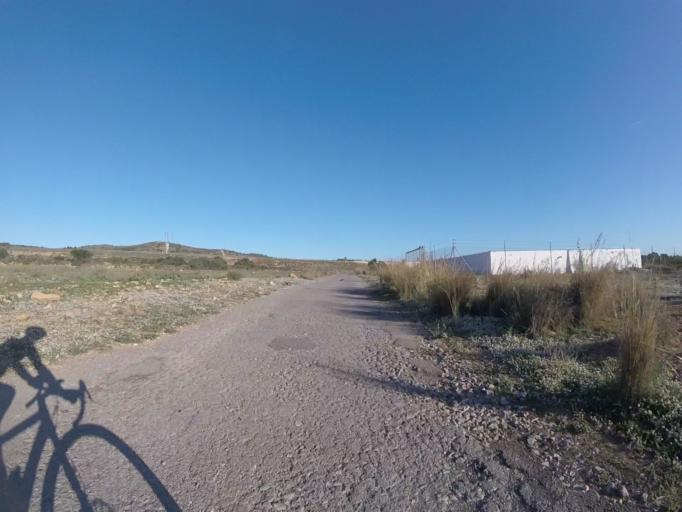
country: ES
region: Valencia
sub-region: Provincia de Castello
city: Torreblanca
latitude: 40.2291
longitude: 0.2010
